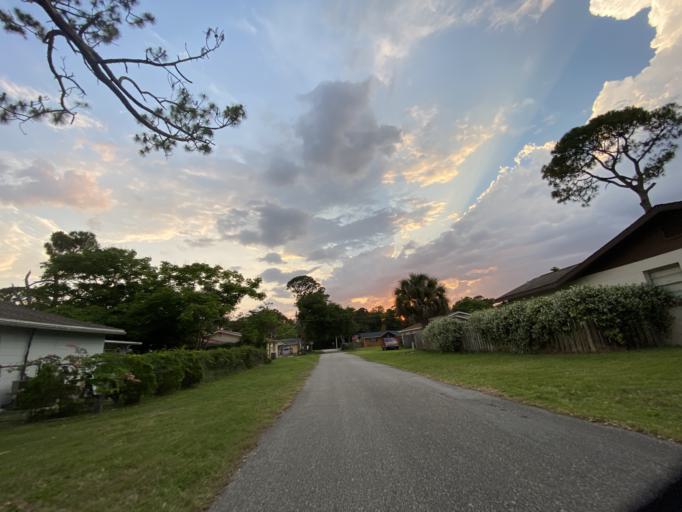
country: US
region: Florida
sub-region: Volusia County
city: Port Orange
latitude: 29.1490
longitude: -80.9967
